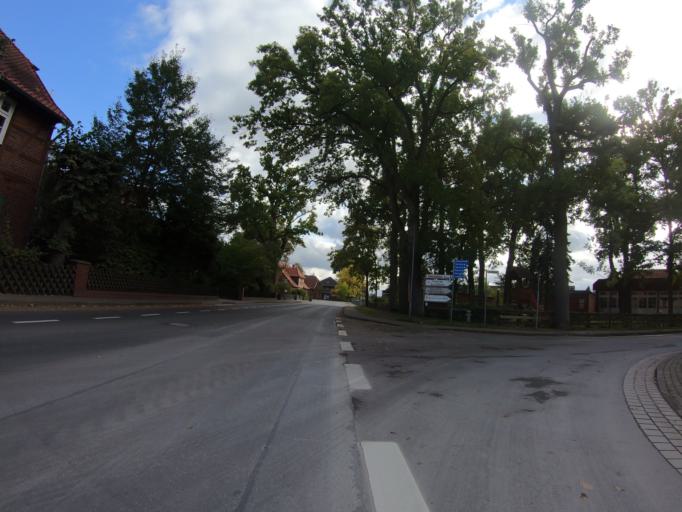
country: DE
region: Lower Saxony
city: Isenbuttel
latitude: 52.4340
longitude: 10.5798
